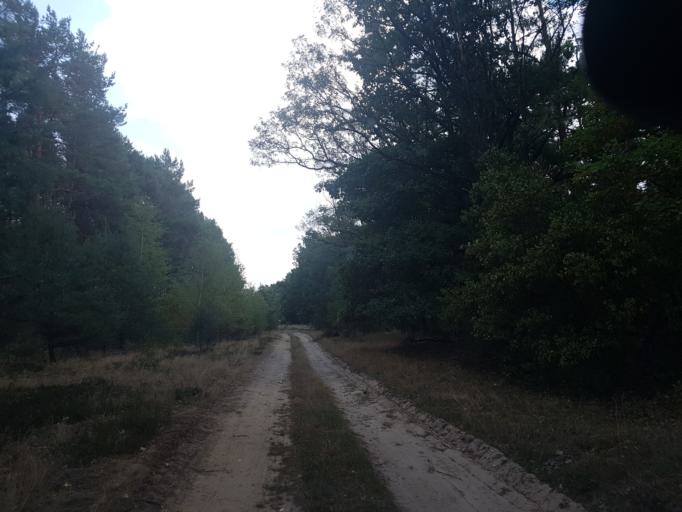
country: DE
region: Brandenburg
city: Treuenbrietzen
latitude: 52.0431
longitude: 12.8589
